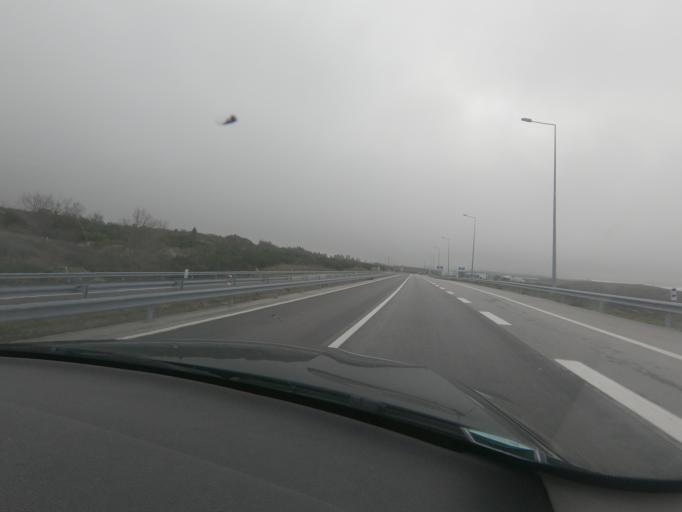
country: PT
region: Viseu
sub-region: Castro Daire
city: Castro Daire
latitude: 40.9701
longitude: -7.8886
